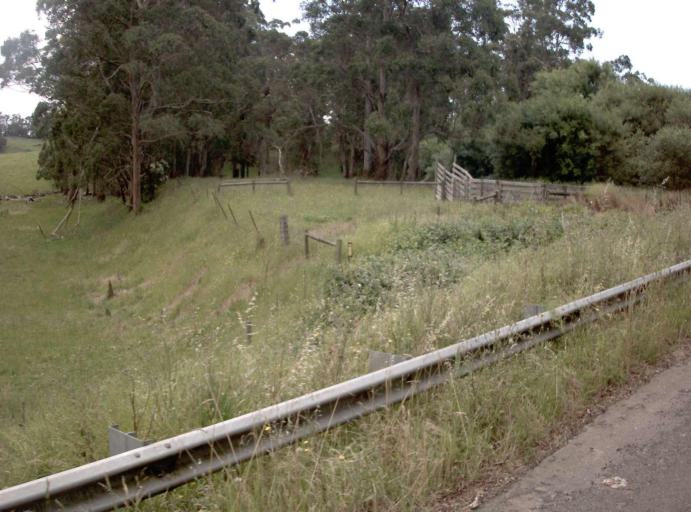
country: AU
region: Victoria
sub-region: Baw Baw
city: Warragul
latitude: -38.0832
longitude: 145.9210
